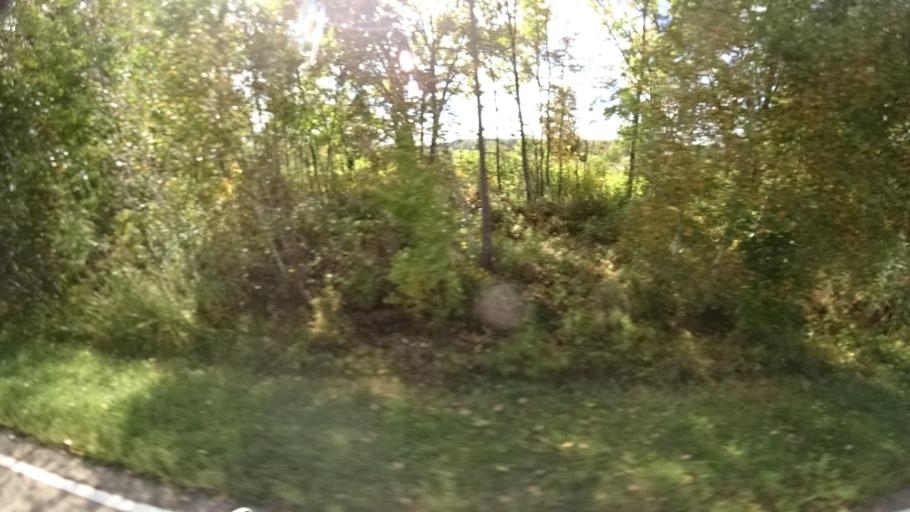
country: RU
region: Primorskiy
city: Yakovlevka
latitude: 44.4185
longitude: 133.5813
